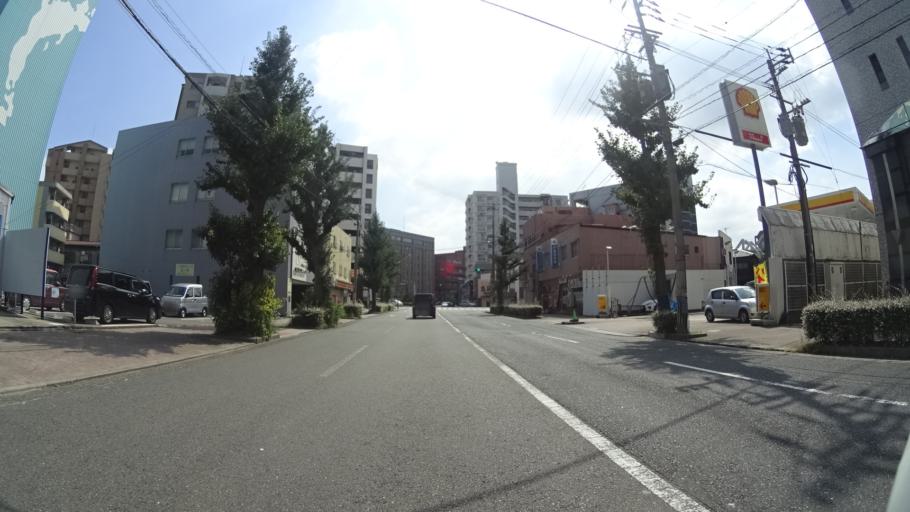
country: JP
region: Fukuoka
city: Kitakyushu
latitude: 33.8791
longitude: 130.8584
